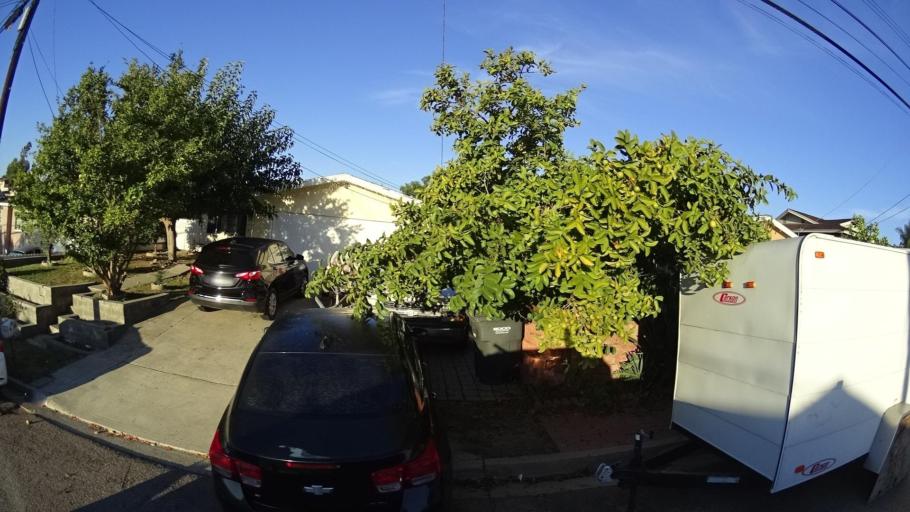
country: US
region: California
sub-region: San Diego County
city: La Presa
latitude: 32.7128
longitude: -116.9931
